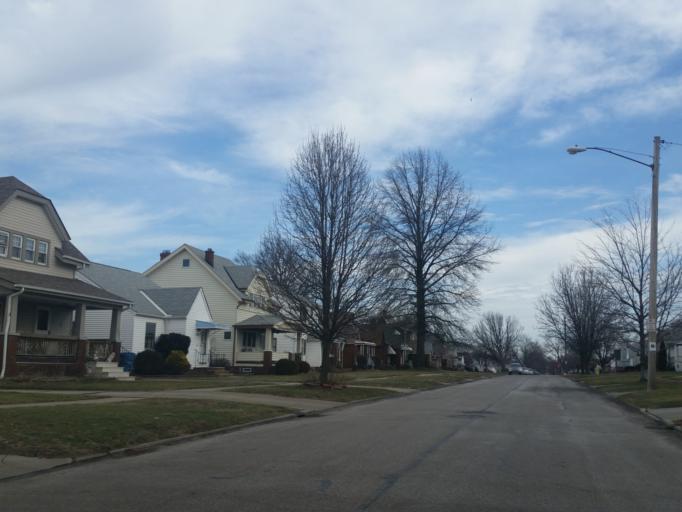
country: US
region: Ohio
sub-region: Cuyahoga County
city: Brooklyn Heights
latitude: 41.4150
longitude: -81.7049
